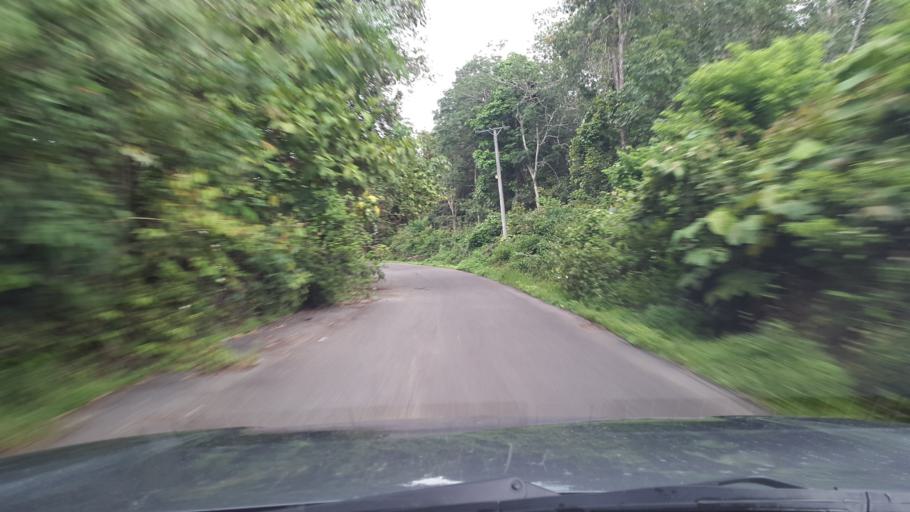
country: ID
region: South Sumatra
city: Gunungmenang
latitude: -3.1668
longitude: 103.9518
